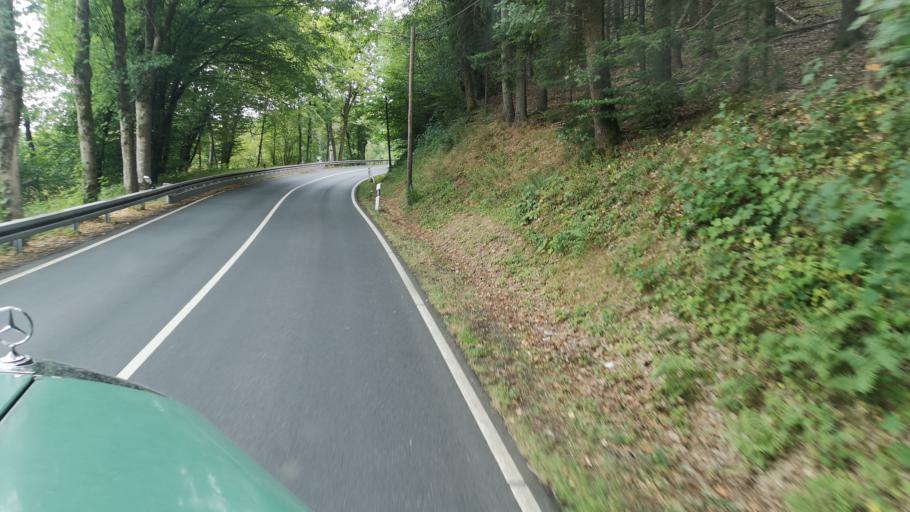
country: DE
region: North Rhine-Westphalia
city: Burscheid
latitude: 51.0730
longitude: 7.1488
